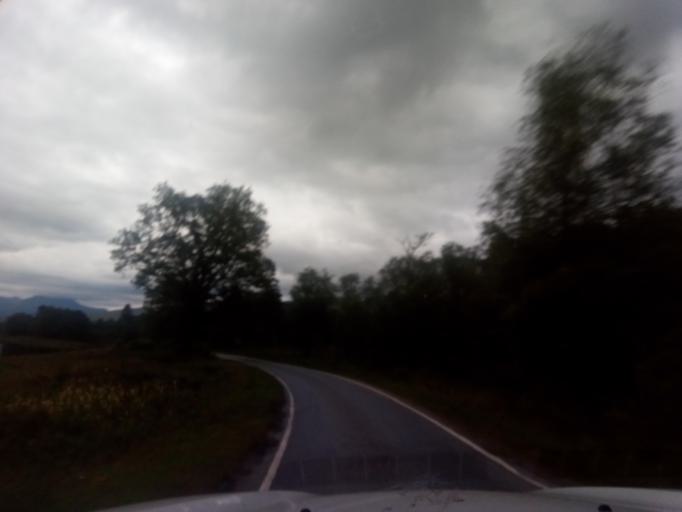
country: GB
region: Scotland
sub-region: Highland
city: Fort William
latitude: 56.8499
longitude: -5.3231
